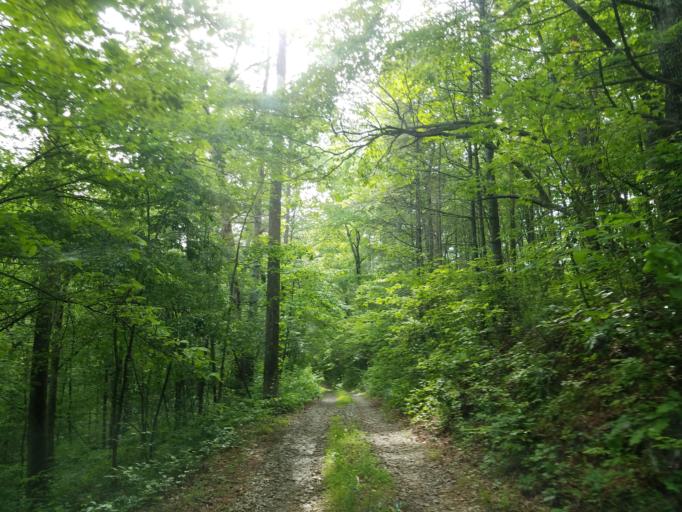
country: US
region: Georgia
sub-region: Union County
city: Blairsville
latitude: 34.7439
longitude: -84.0145
